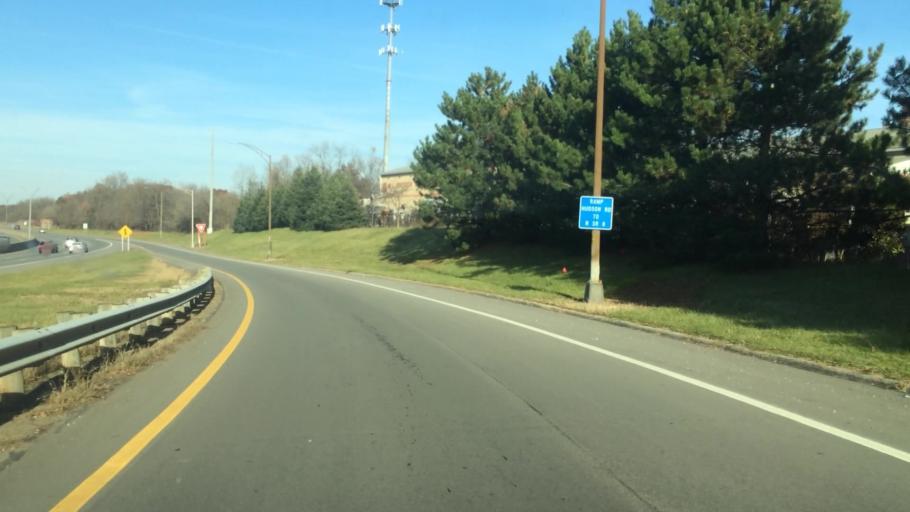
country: US
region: Ohio
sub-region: Summit County
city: Cuyahoga Falls
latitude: 41.1486
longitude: -81.4727
